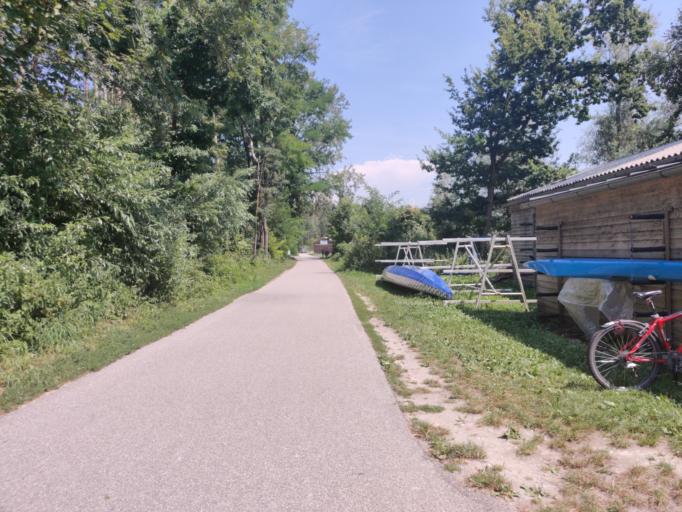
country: AT
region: Upper Austria
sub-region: Politischer Bezirk Urfahr-Umgebung
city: Ottensheim
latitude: 48.3268
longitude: 14.1586
